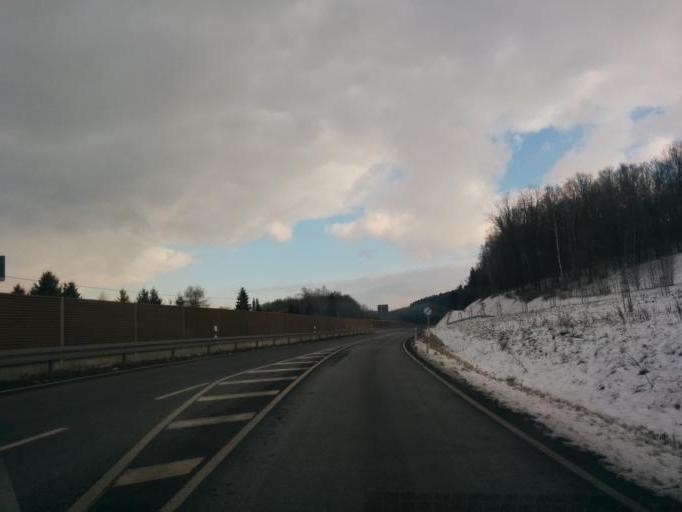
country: DE
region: Saxony
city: Niederwiesa
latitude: 50.8629
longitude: 13.0408
